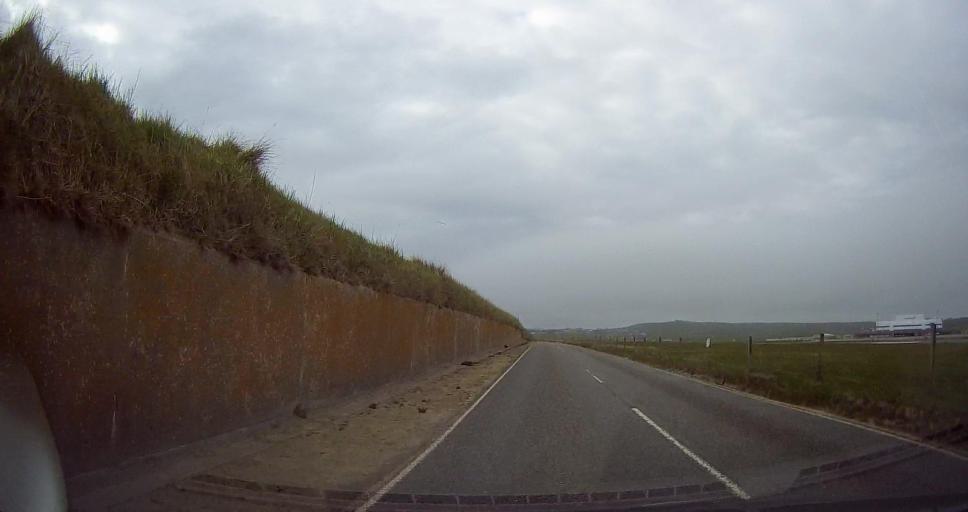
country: GB
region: Scotland
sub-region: Shetland Islands
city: Sandwick
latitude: 59.8728
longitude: -1.2887
